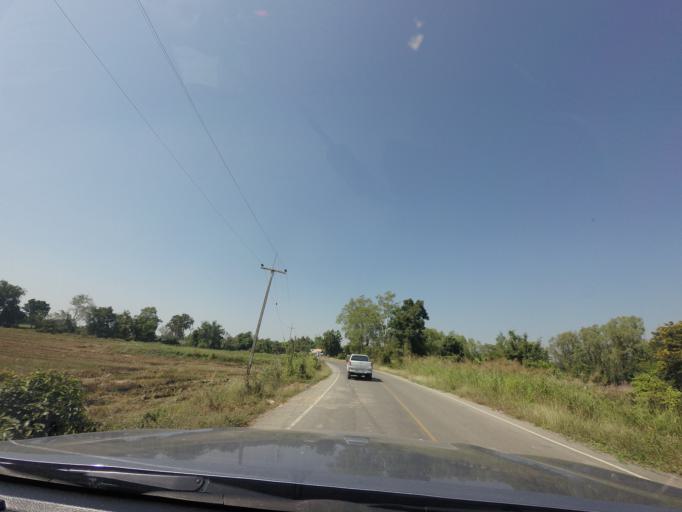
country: TH
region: Sukhothai
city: Si Samrong
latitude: 17.1309
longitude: 99.7794
